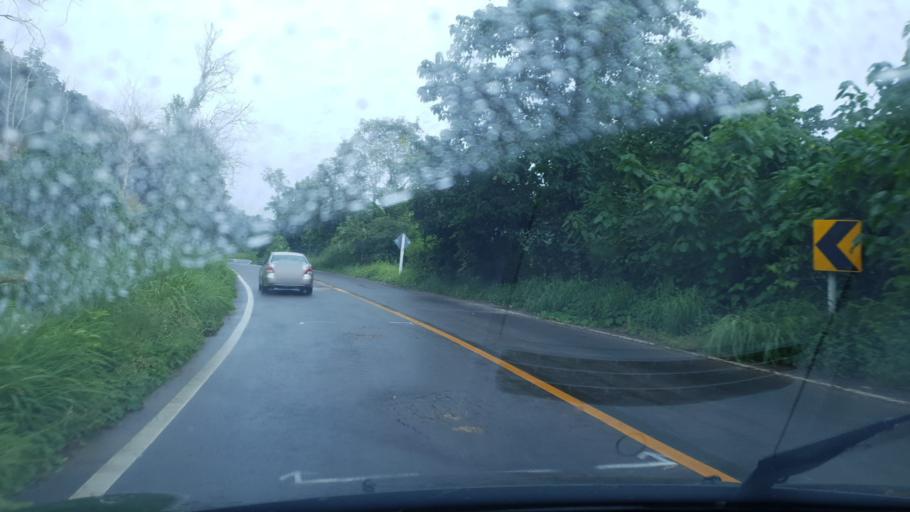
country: TH
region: Mae Hong Son
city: Khun Yuam
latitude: 18.6836
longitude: 97.9197
